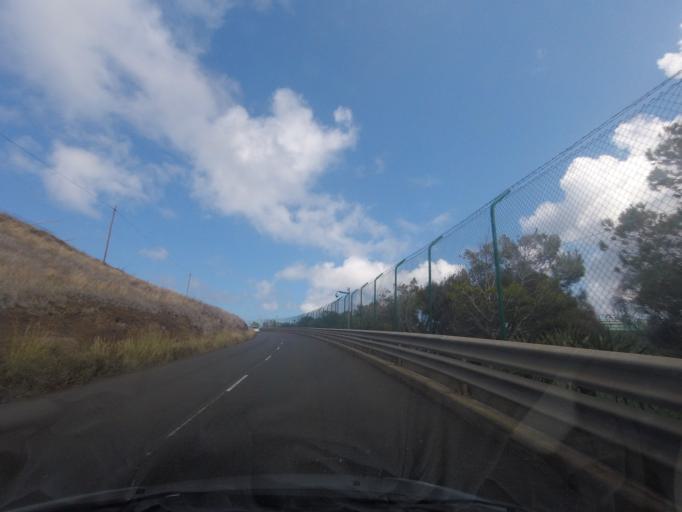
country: PT
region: Madeira
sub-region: Machico
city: Canical
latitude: 32.7437
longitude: -16.7297
